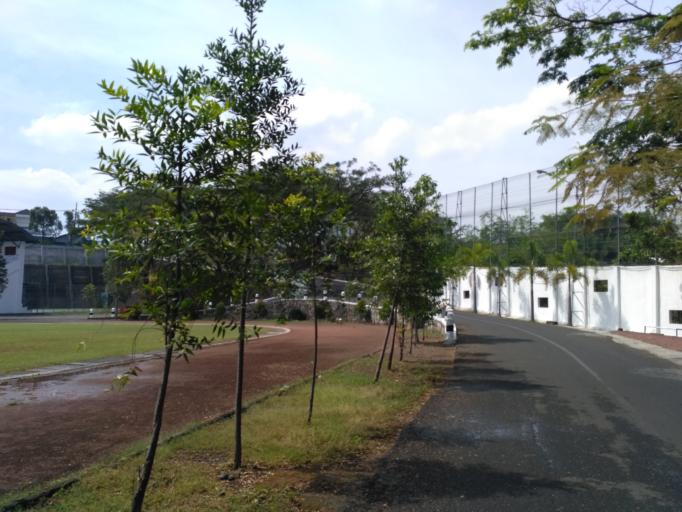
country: ID
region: East Java
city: Malang
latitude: -7.9236
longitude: 112.6006
